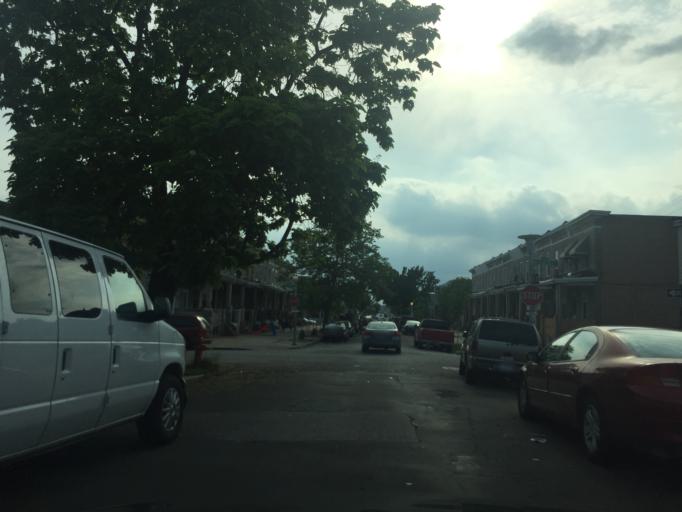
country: US
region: Maryland
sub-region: City of Baltimore
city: Baltimore
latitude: 39.2982
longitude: -76.5704
